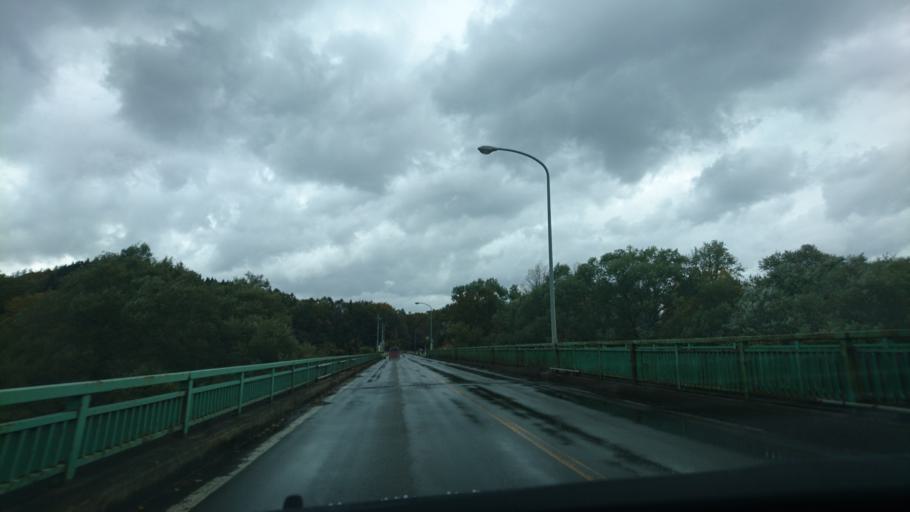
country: JP
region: Iwate
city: Shizukuishi
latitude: 39.6646
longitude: 140.9697
